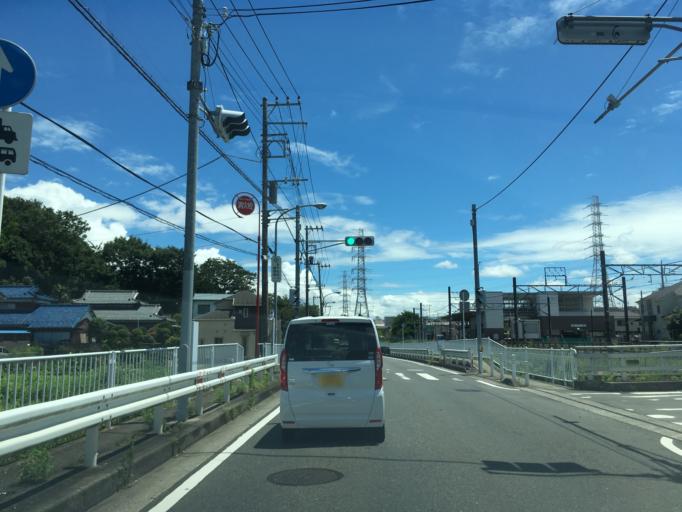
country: JP
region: Tokyo
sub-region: Machida-shi
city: Machida
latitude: 35.5467
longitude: 139.4916
